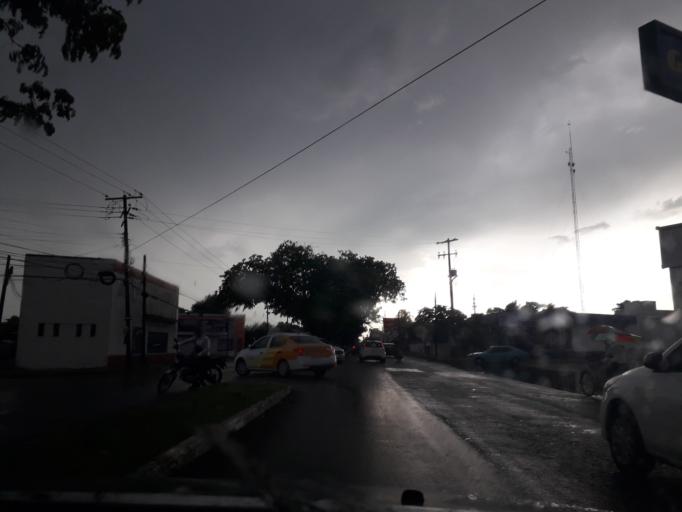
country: MX
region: Yucatan
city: Merida
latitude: 20.9808
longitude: -89.6494
